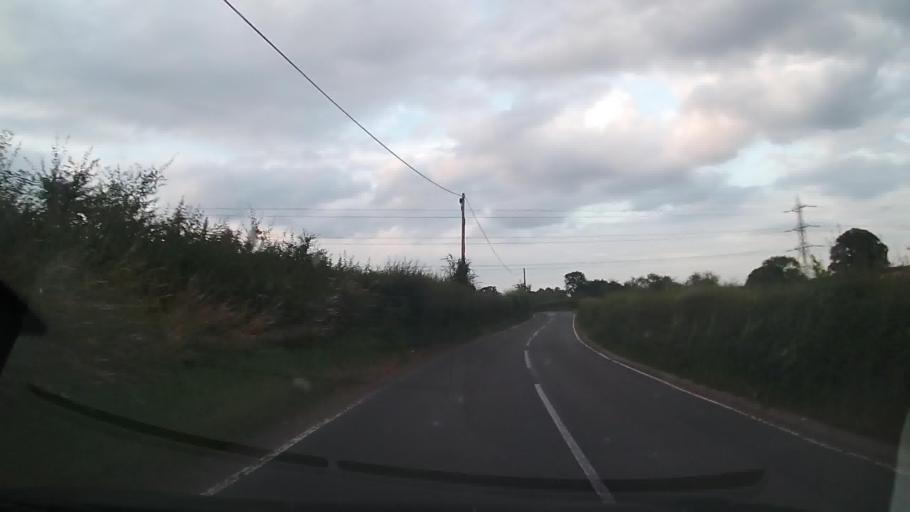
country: GB
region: England
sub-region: Shropshire
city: Petton
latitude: 52.8013
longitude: -2.8449
